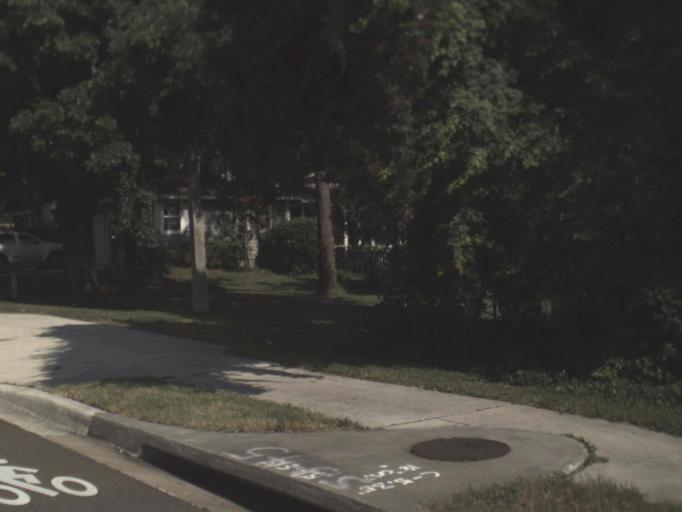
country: US
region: Florida
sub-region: Duval County
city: Atlantic Beach
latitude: 30.3587
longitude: -81.4707
